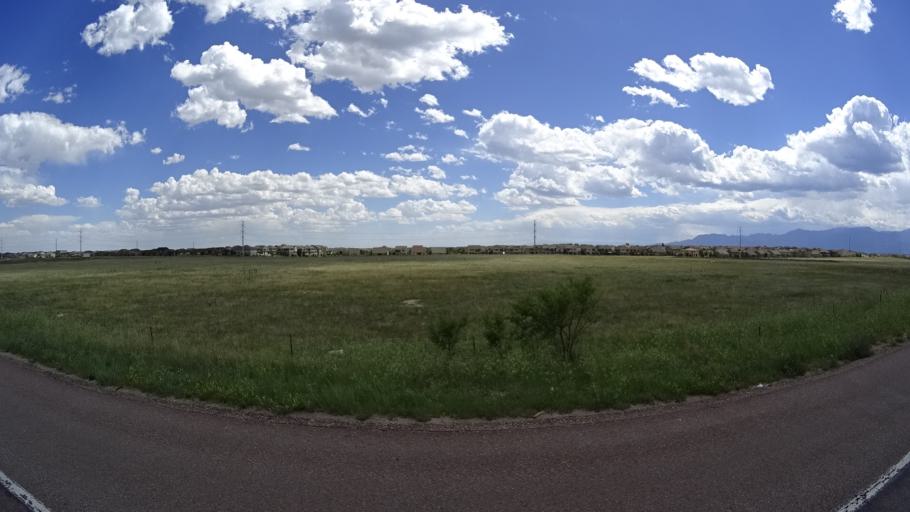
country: US
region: Colorado
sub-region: El Paso County
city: Black Forest
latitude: 38.9405
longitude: -104.6725
